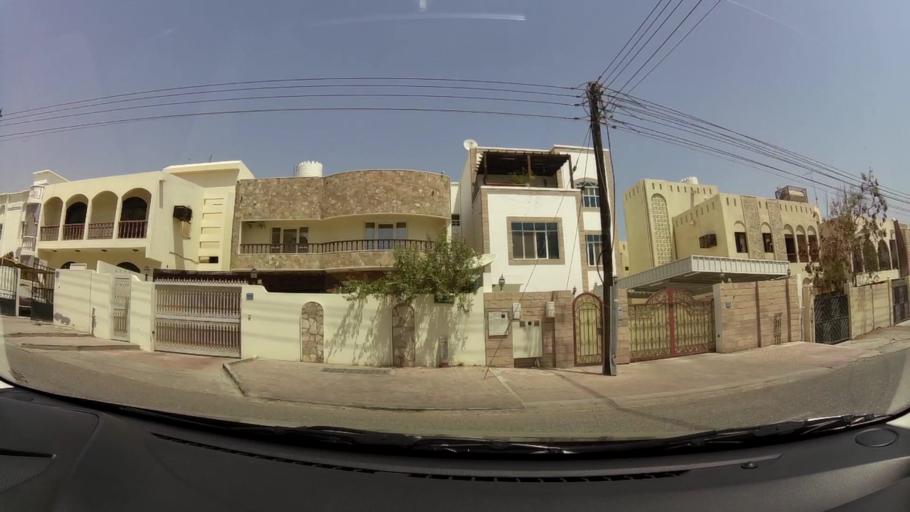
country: OM
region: Muhafazat Masqat
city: Bawshar
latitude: 23.5922
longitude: 58.4314
